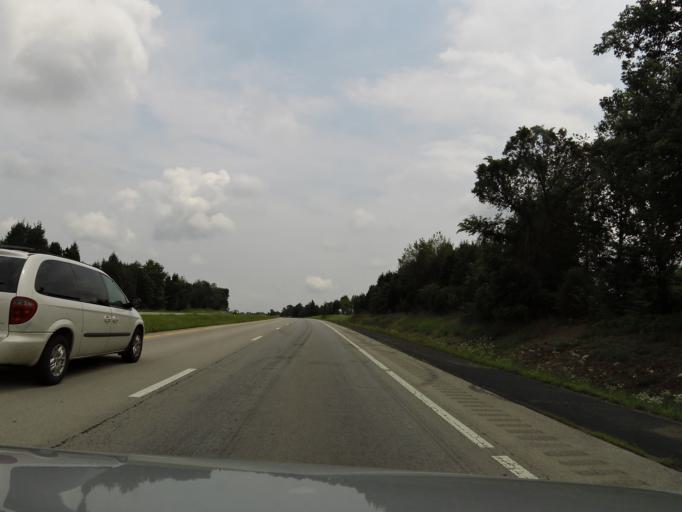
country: US
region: Kentucky
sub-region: Hardin County
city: Elizabethtown
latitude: 37.5633
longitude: -86.0580
